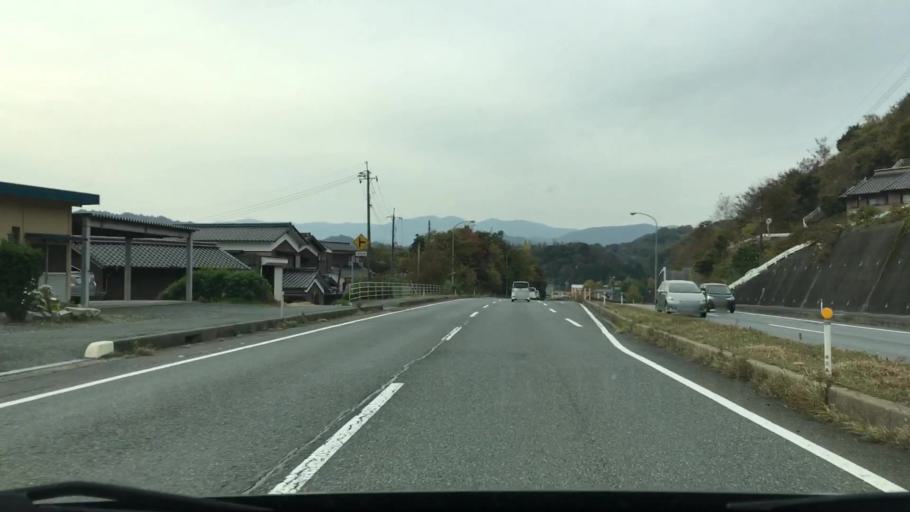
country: JP
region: Yamaguchi
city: Tokuyama
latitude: 34.0744
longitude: 131.7416
